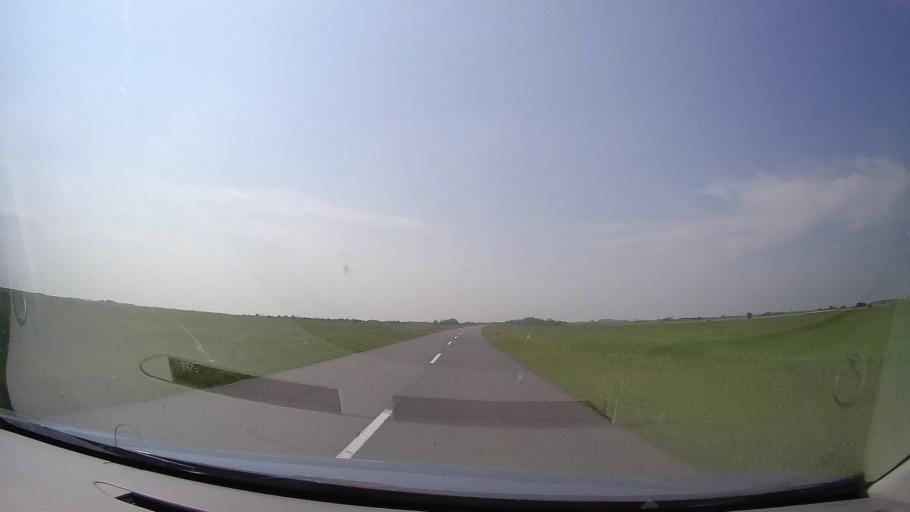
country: RS
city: Jarkovac
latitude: 45.2987
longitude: 20.7629
